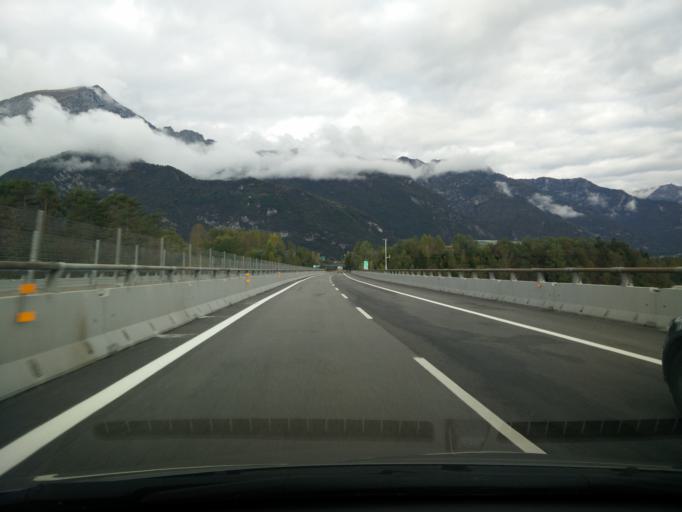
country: IT
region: Veneto
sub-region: Provincia di Belluno
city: Soccher-Paiane-Casan-Arsie
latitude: 46.1765
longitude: 12.3013
